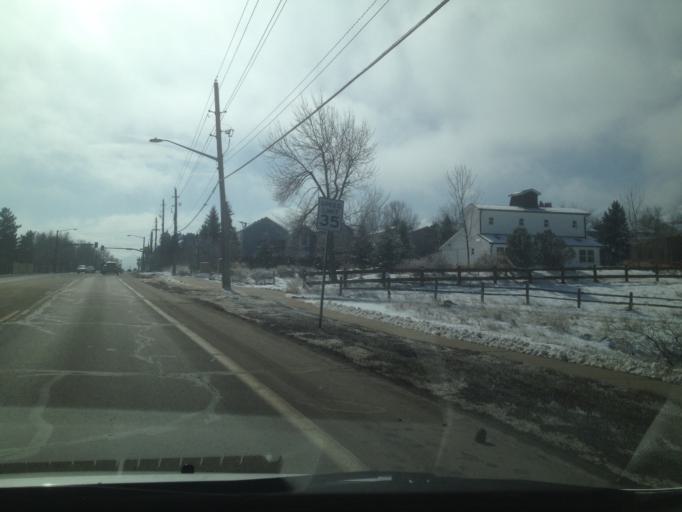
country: US
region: Colorado
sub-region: Boulder County
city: Boulder
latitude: 40.0495
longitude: -105.2822
